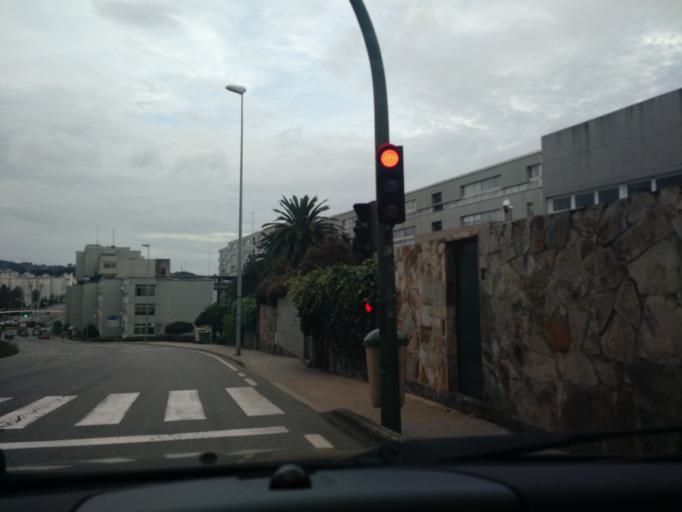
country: ES
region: Galicia
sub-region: Provincia da Coruna
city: A Coruna
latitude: 43.3430
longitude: -8.4014
